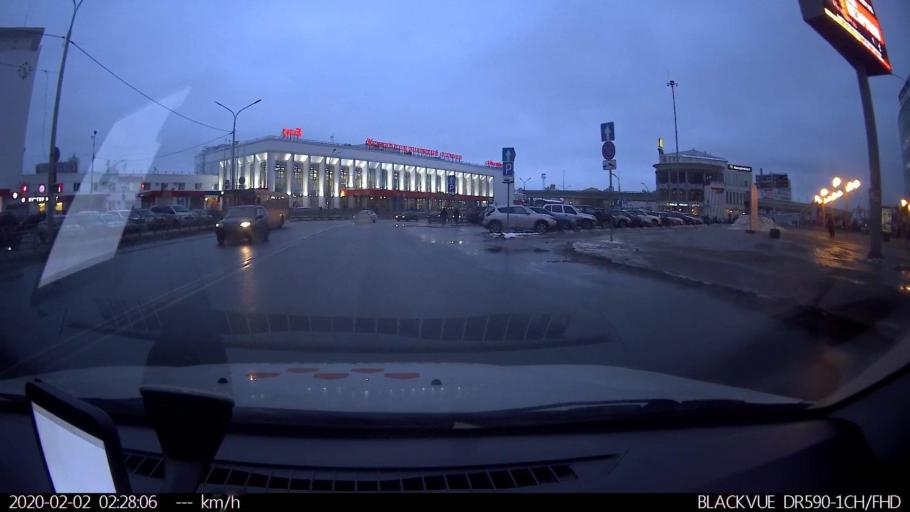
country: RU
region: Nizjnij Novgorod
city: Nizhniy Novgorod
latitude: 56.2815
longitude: 43.9750
